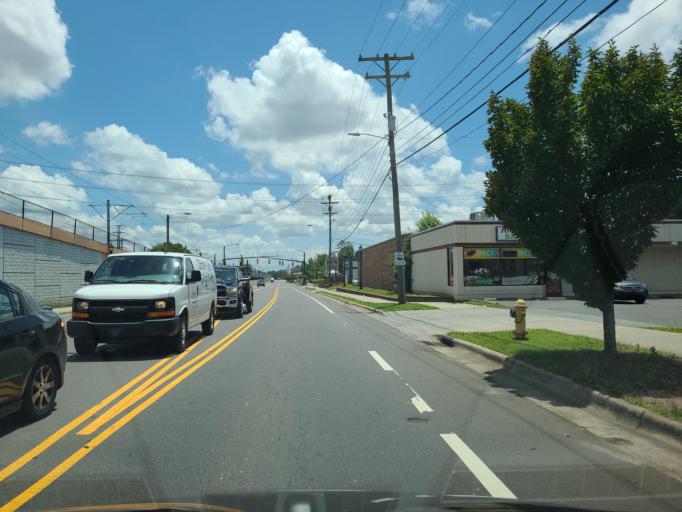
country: US
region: North Carolina
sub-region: Mecklenburg County
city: Charlotte
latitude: 35.1773
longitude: -80.8797
